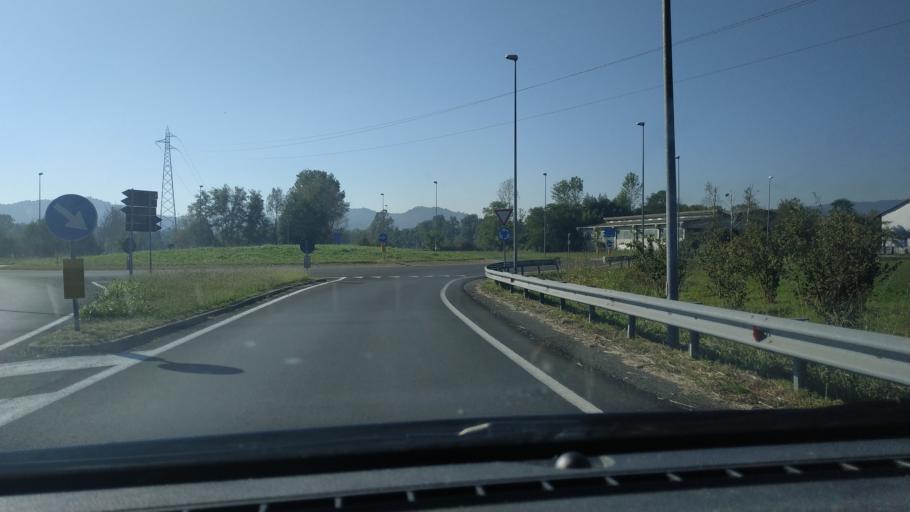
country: IT
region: Piedmont
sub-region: Provincia di Torino
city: Verolengo
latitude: 45.1840
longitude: 7.9596
